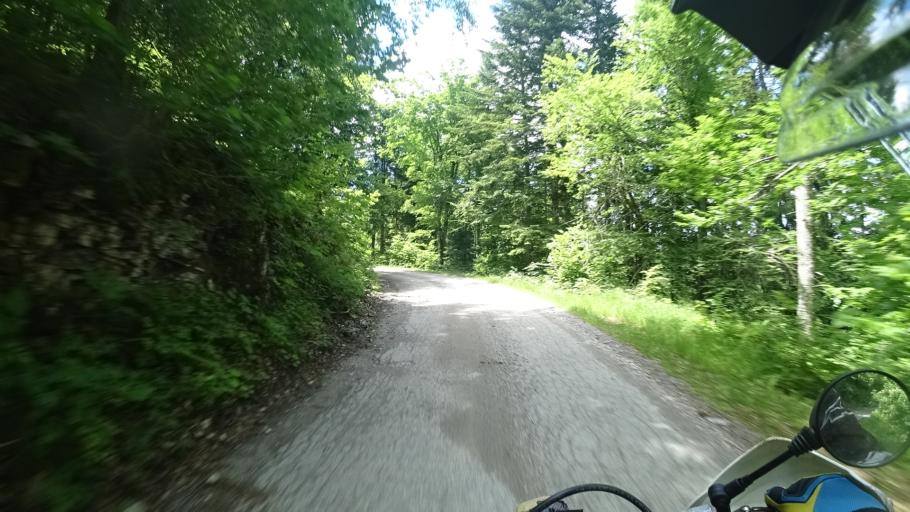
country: SI
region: Loski Potok
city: Hrib-Loski Potok
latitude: 45.6123
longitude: 14.5705
